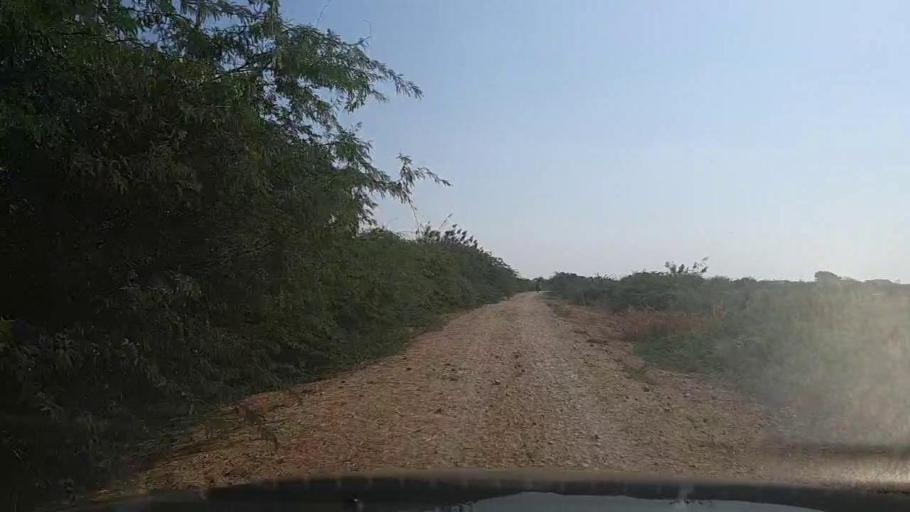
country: PK
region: Sindh
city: Gharo
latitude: 24.7110
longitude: 67.7452
